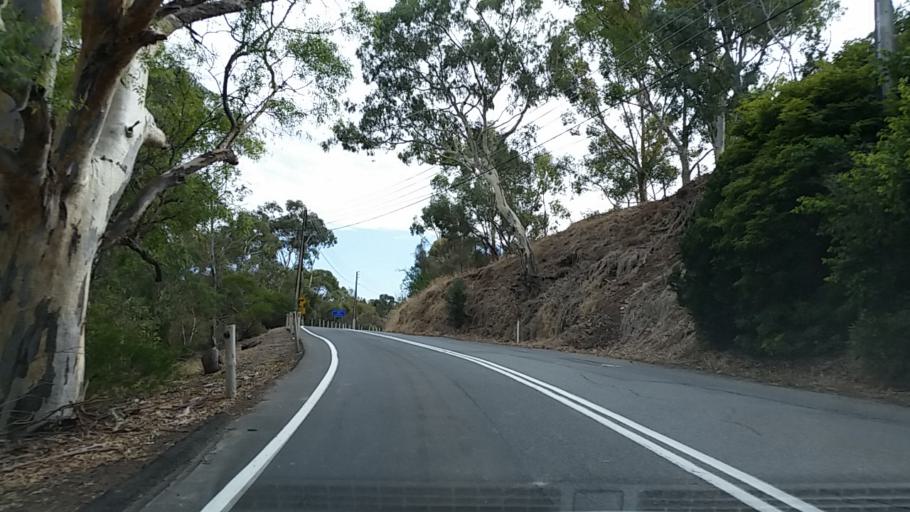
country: AU
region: South Australia
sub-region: Campbelltown
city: Athelstone
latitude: -34.8615
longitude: 138.7213
